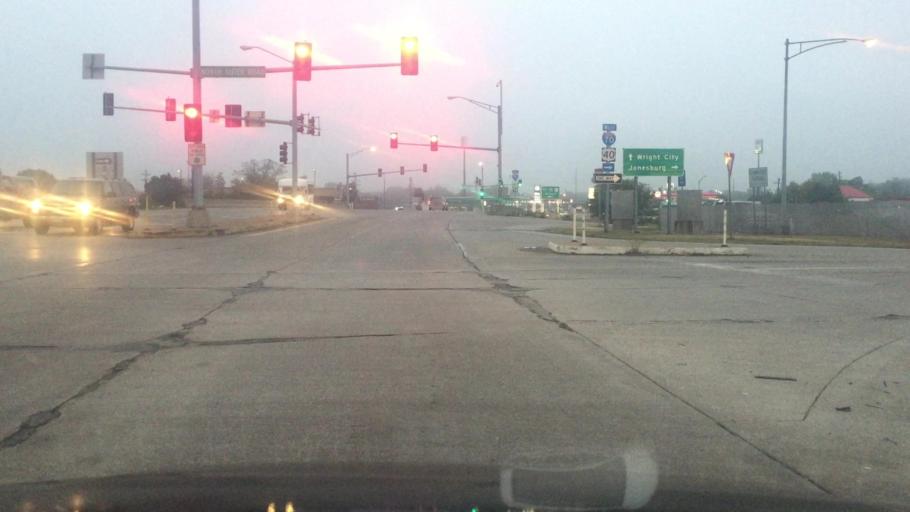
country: US
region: Missouri
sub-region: Warren County
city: Warrenton
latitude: 38.8223
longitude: -91.1387
